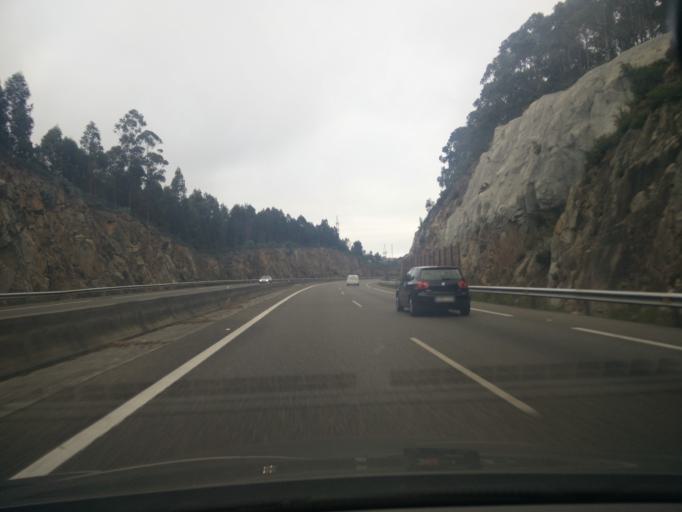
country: ES
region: Galicia
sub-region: Provincia da Coruna
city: Arteixo
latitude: 43.3224
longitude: -8.4674
